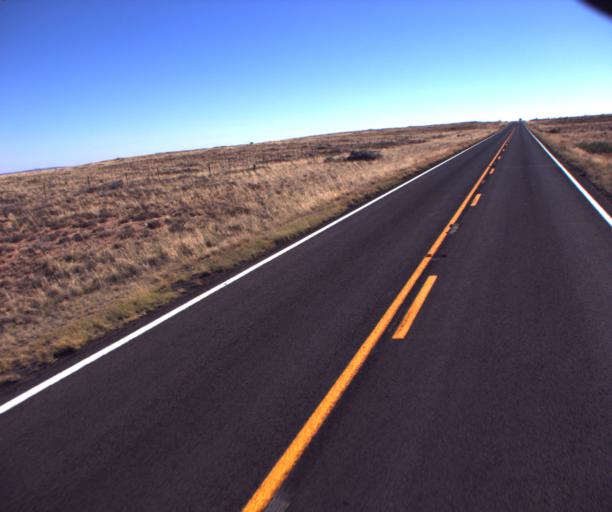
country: US
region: Arizona
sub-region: Coconino County
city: Tuba City
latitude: 35.9723
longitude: -110.9673
